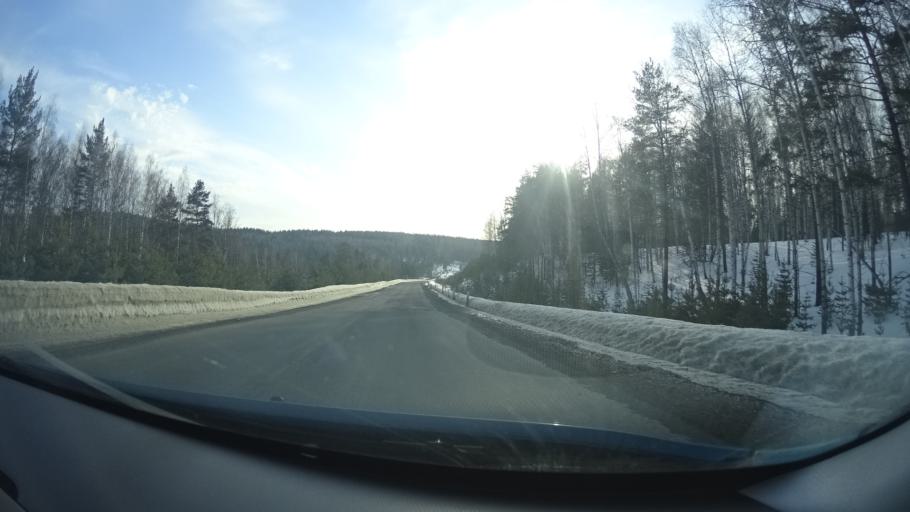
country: RU
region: Bashkortostan
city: Lomovka
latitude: 53.6747
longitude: 58.2449
